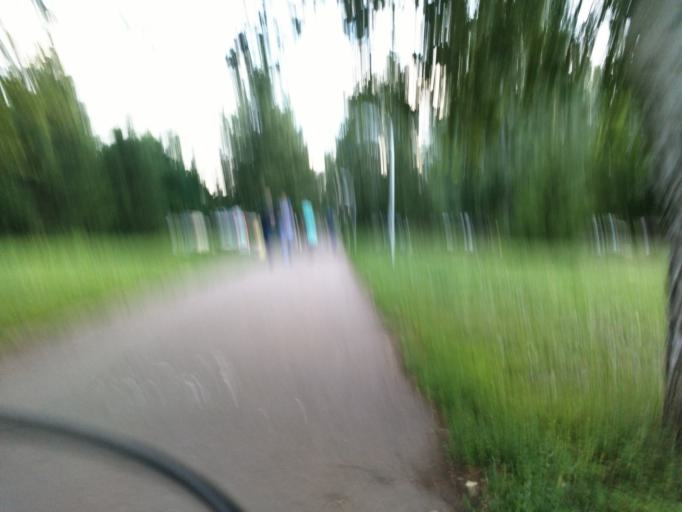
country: RU
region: Tatarstan
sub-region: Tukayevskiy Rayon
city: Naberezhnyye Chelny
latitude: 55.7483
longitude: 52.4158
